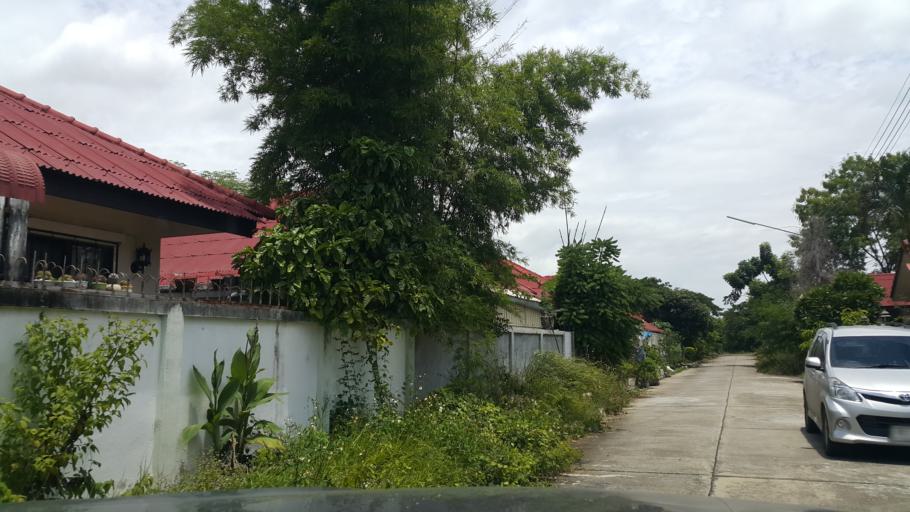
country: TH
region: Chiang Mai
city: Hang Dong
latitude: 18.7071
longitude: 98.9690
